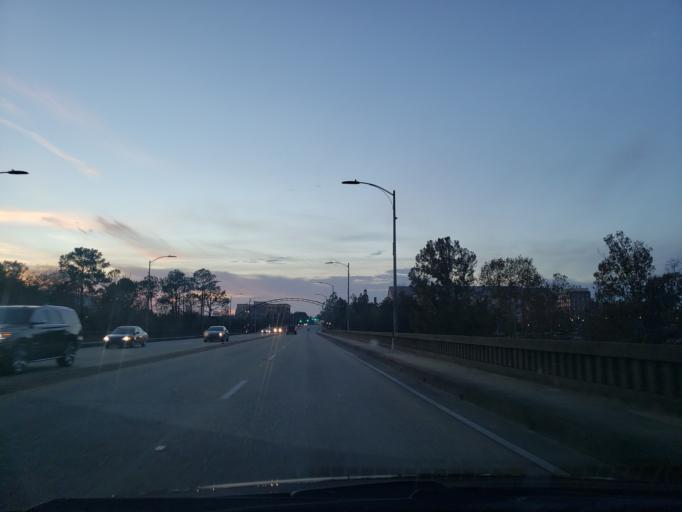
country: US
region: Georgia
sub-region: Dougherty County
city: Albany
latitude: 31.5755
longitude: -84.1469
